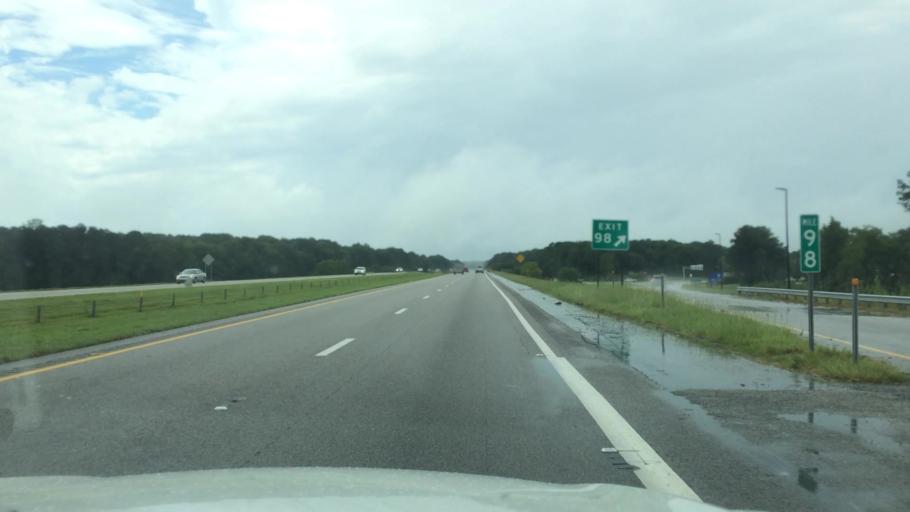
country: US
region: South Carolina
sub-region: Kershaw County
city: Camden
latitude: 34.2167
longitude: -80.5889
